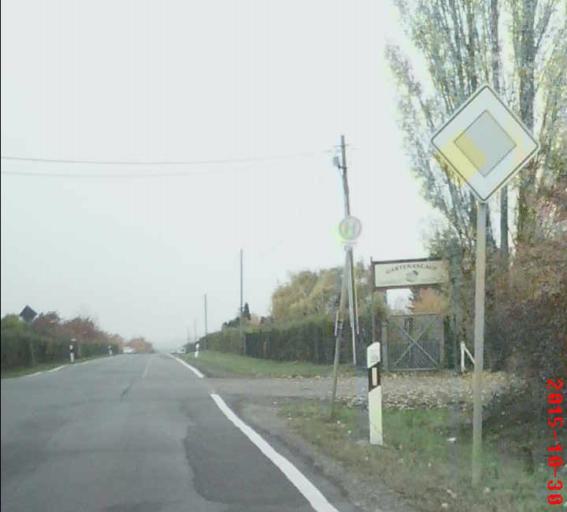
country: DE
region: Thuringia
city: Muehlhausen
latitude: 51.2270
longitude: 10.4259
